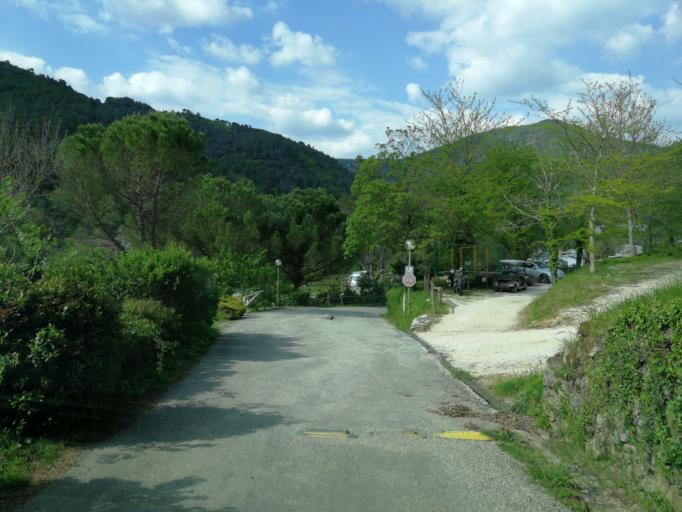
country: FR
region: Rhone-Alpes
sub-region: Departement de l'Ardeche
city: Saint-Sauveur-de-Montagut
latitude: 44.8070
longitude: 4.6150
